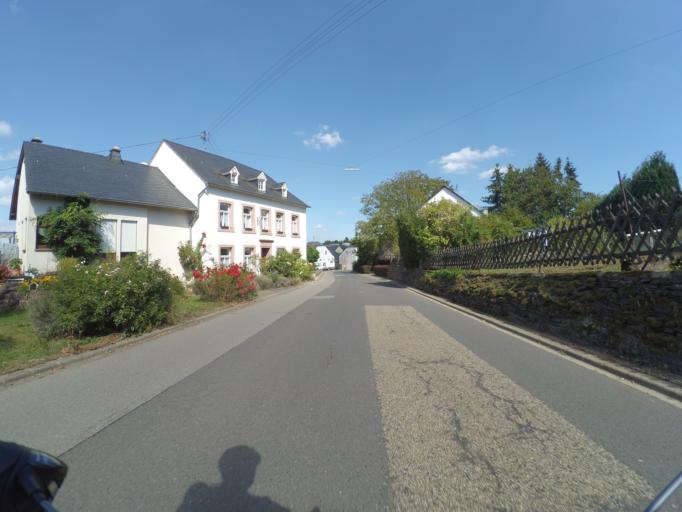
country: DE
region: Rheinland-Pfalz
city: Heidenburg
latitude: 49.7962
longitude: 6.9171
